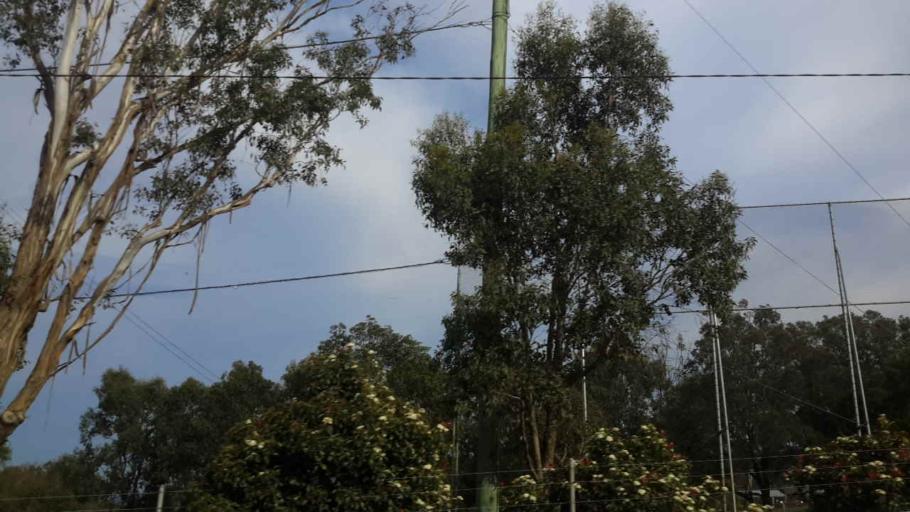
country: AU
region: New South Wales
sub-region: Penrith Municipality
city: Kingswood Park
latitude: -33.7885
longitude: 150.7011
